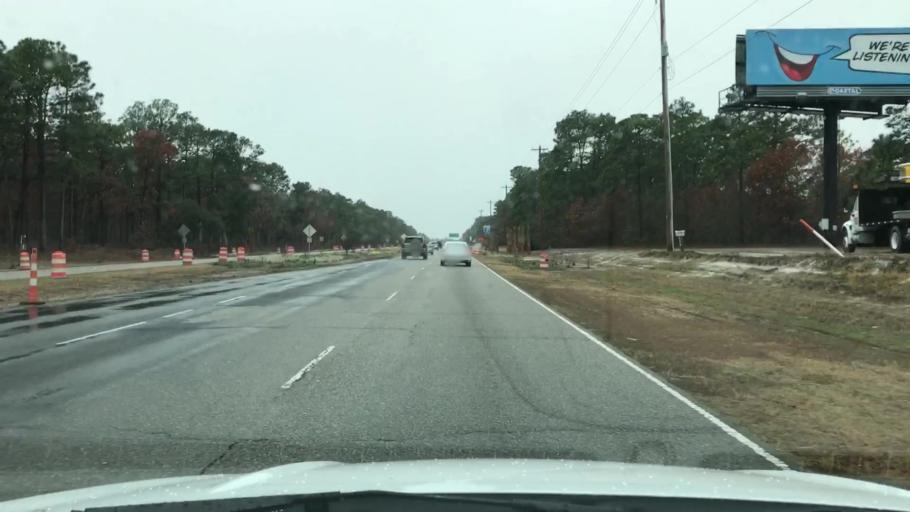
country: US
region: South Carolina
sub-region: Horry County
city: Myrtle Beach
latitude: 33.7529
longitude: -78.8294
